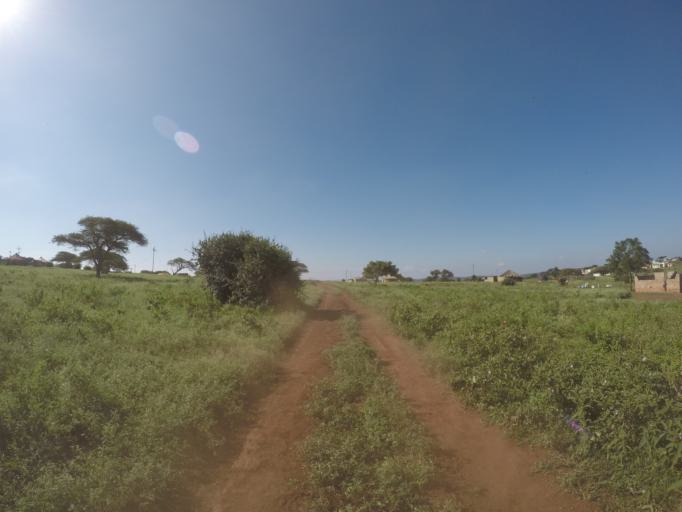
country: ZA
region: KwaZulu-Natal
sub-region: uThungulu District Municipality
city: Empangeni
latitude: -28.5733
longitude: 31.7283
